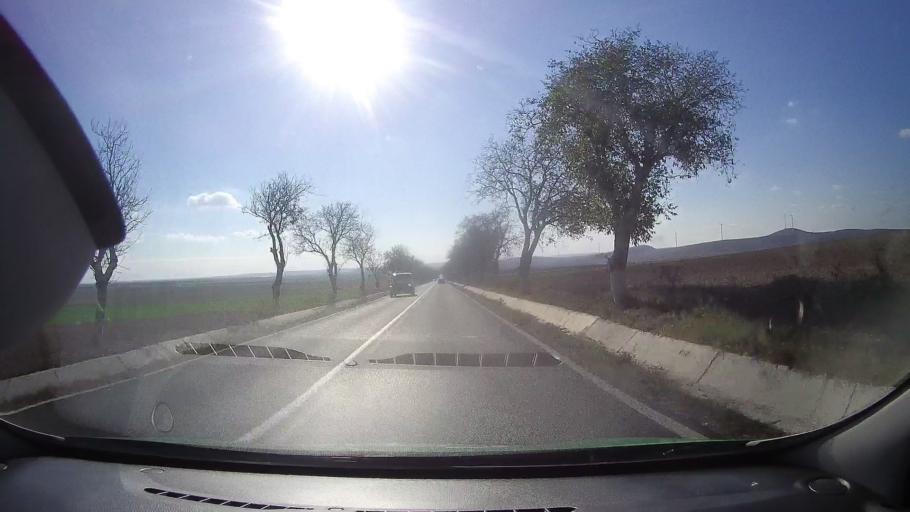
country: RO
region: Tulcea
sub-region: Comuna Ceamurlia de Jos
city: Ceamurlia de Jos
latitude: 44.8055
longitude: 28.6908
